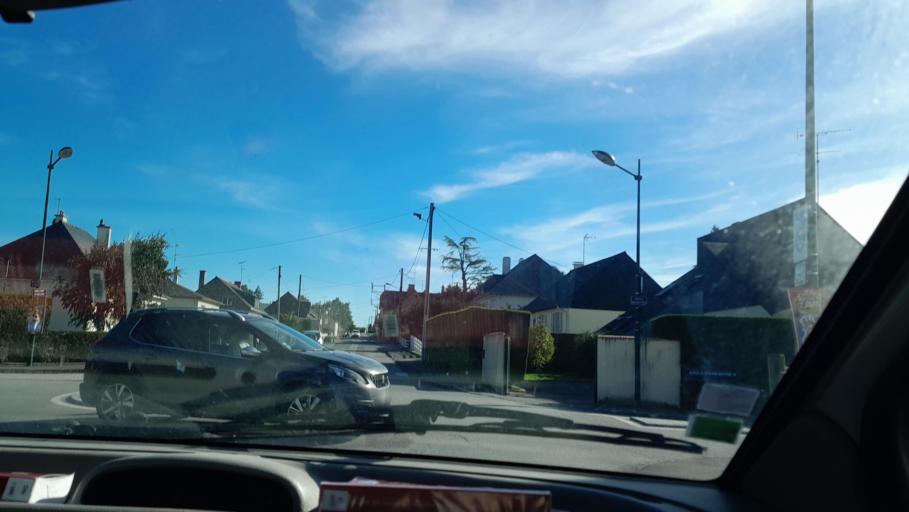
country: FR
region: Brittany
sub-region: Departement d'Ille-et-Vilaine
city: Argentre-du-Plessis
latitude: 48.0538
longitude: -1.1502
